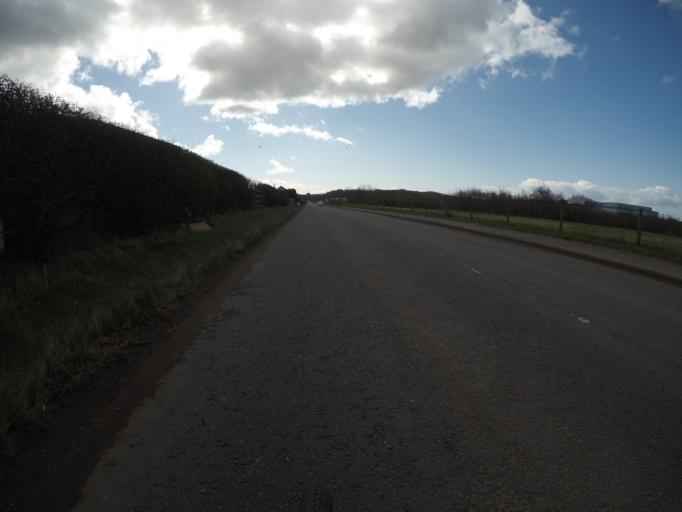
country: GB
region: Scotland
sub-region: North Ayrshire
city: Dreghorn
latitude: 55.5901
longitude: -4.6018
